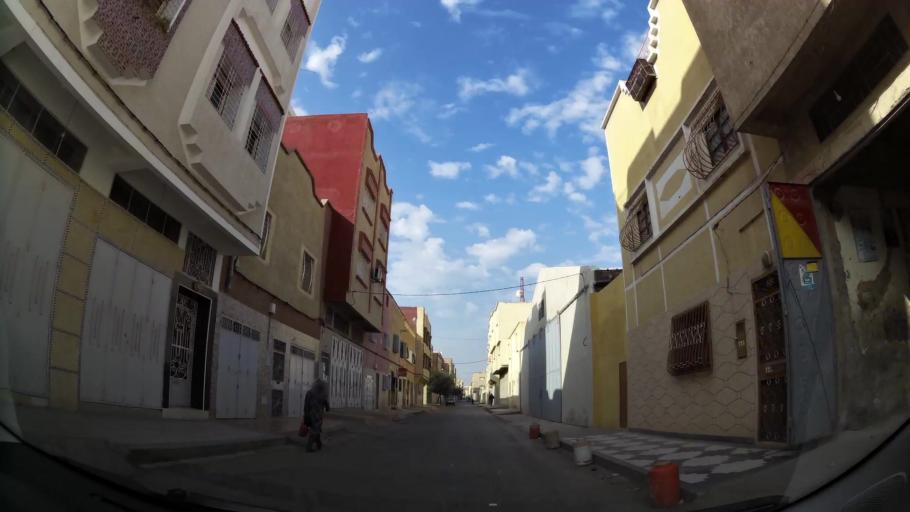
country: MA
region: Oriental
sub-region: Oujda-Angad
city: Oujda
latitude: 34.6931
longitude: -1.9050
